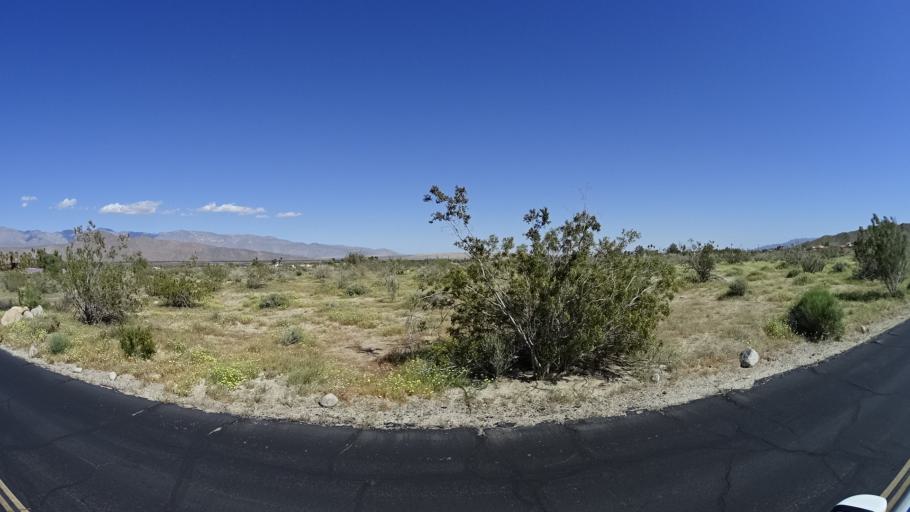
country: US
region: California
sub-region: San Diego County
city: Borrego Springs
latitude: 33.2662
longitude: -116.4025
